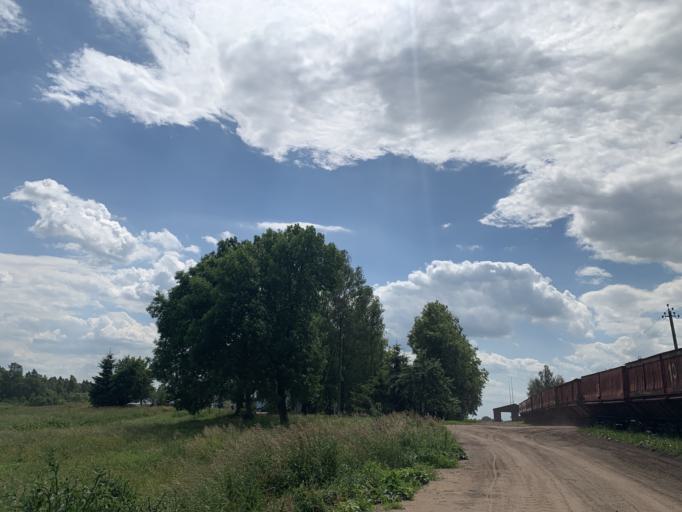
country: BY
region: Minsk
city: Nyasvizh
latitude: 53.2153
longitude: 26.7363
